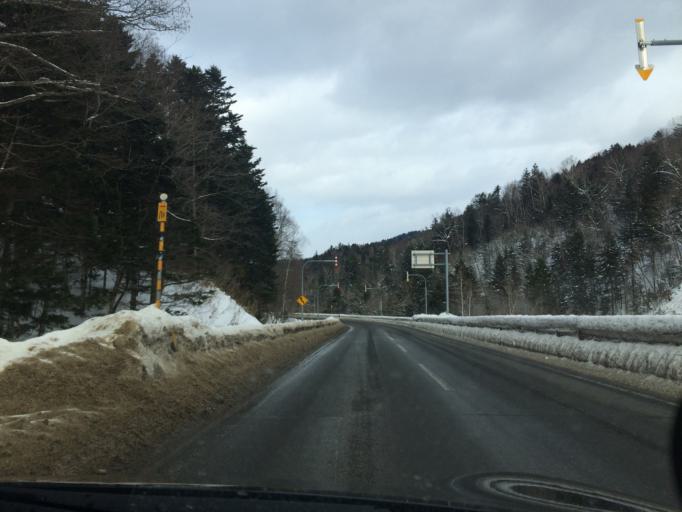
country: JP
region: Hokkaido
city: Shimo-furano
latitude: 42.9391
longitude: 142.3734
